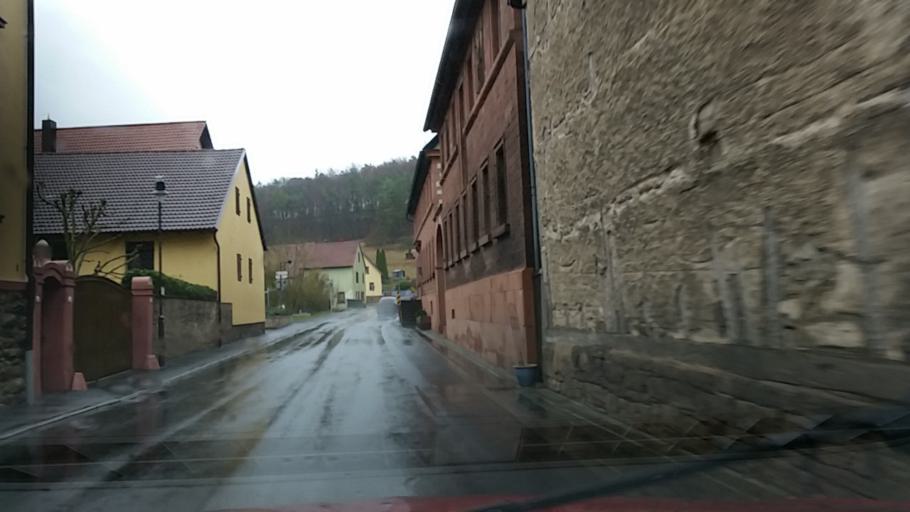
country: DE
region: Bavaria
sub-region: Regierungsbezirk Unterfranken
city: Birkenfeld
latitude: 49.8727
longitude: 9.7211
